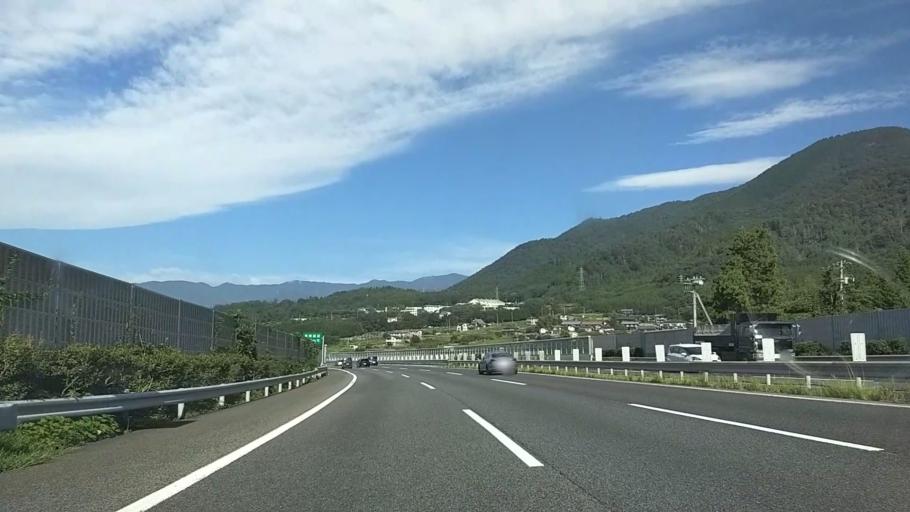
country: JP
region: Yamanashi
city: Otsuki
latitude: 35.6196
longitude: 138.9935
